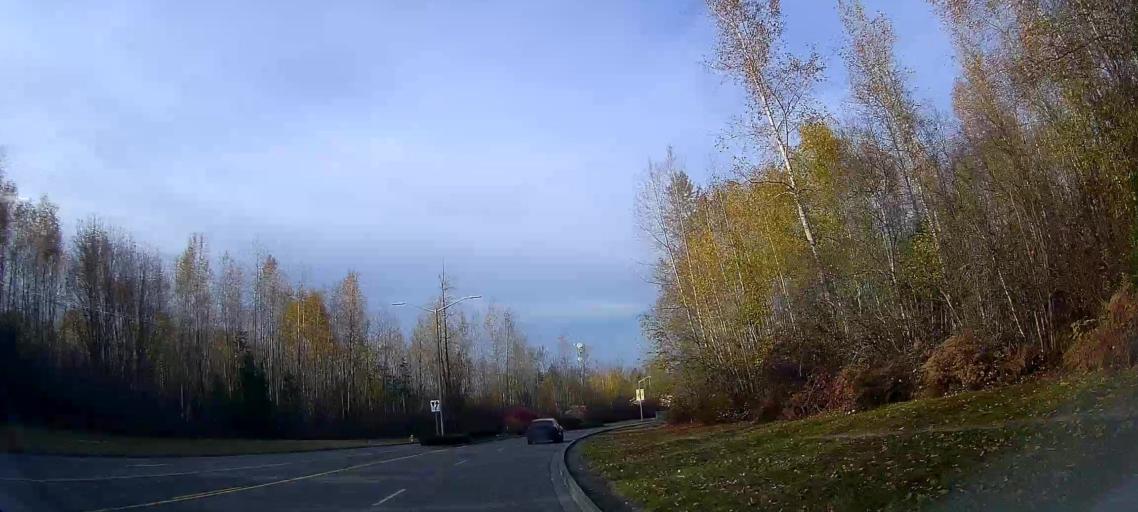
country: US
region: Washington
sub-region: Snohomish County
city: Marysville
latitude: 48.0969
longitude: -122.1914
